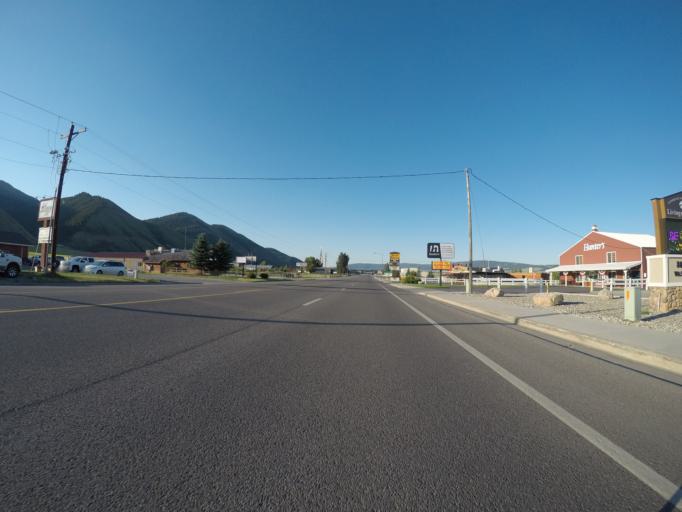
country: US
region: Wyoming
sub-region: Lincoln County
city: Afton
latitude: 42.7161
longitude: -110.9336
